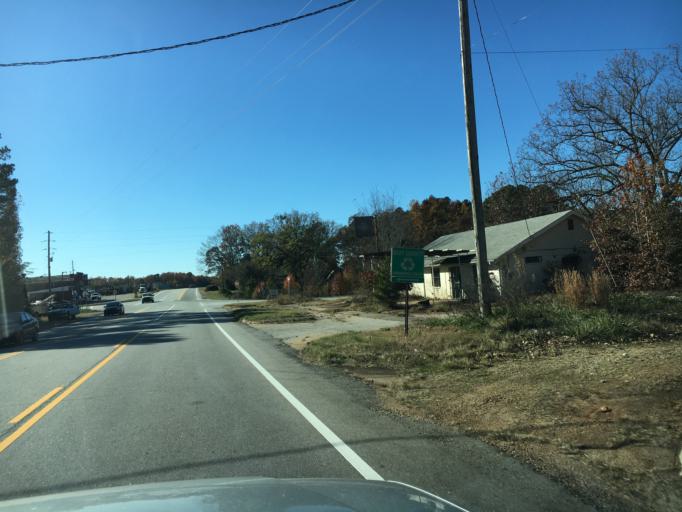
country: US
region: Georgia
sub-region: Hart County
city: Royston
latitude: 34.2908
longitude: -83.0456
